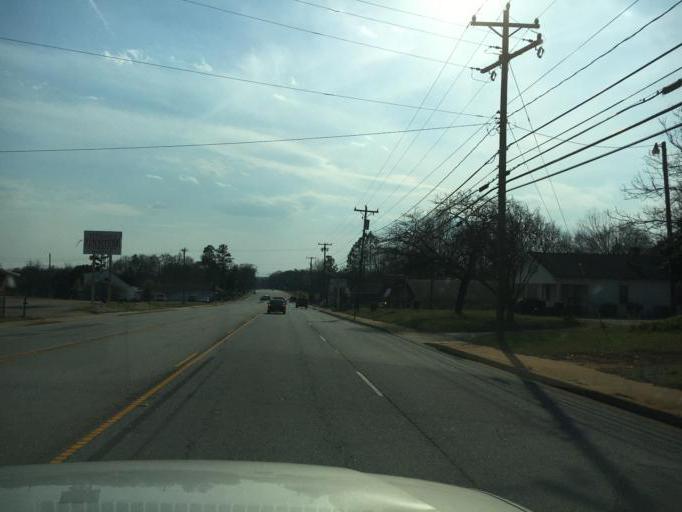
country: US
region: South Carolina
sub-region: Spartanburg County
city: Spartanburg
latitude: 34.9929
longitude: -81.9161
